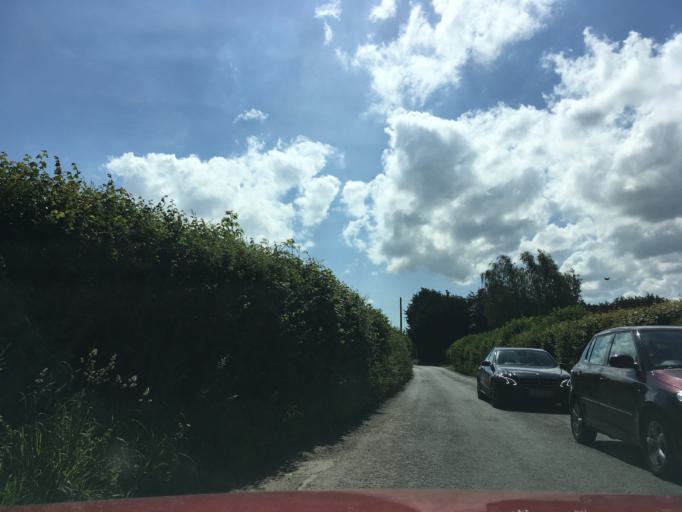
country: GB
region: England
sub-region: Gloucestershire
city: Dursley
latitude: 51.7338
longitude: -2.3888
